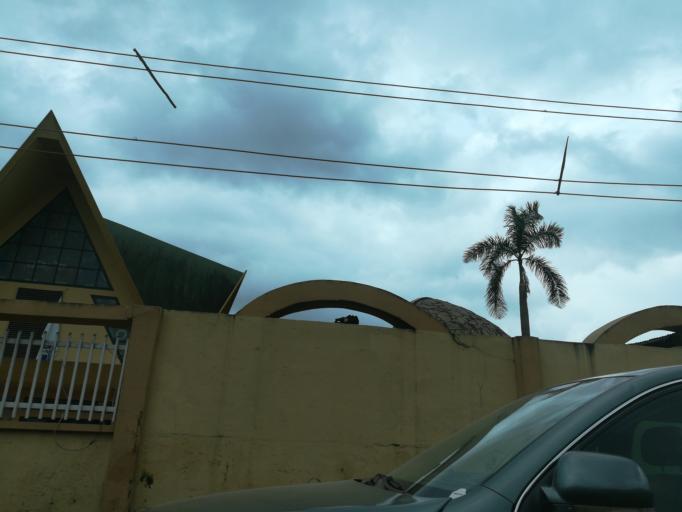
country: NG
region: Lagos
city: Oshodi
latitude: 6.5545
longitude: 3.3299
